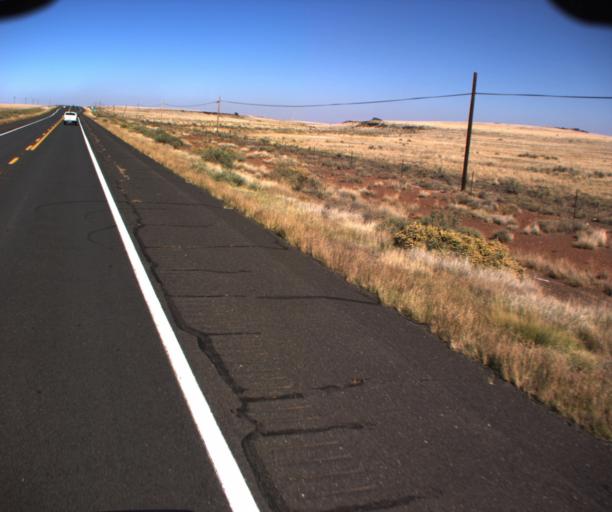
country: US
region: Arizona
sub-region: Coconino County
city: Flagstaff
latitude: 35.6420
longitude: -111.5178
